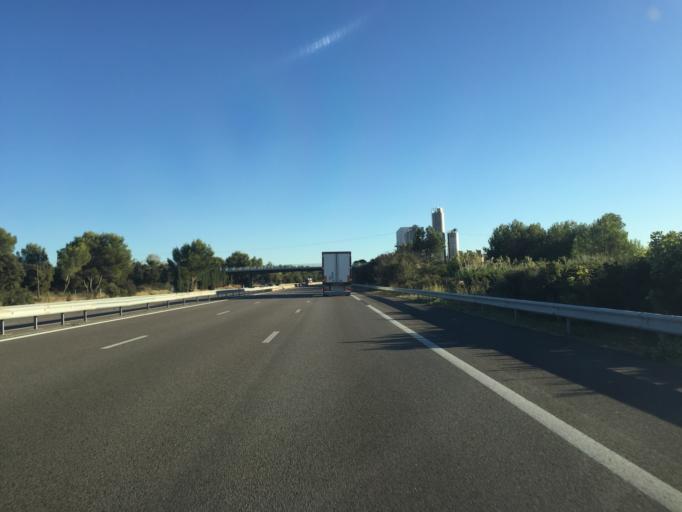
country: FR
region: Provence-Alpes-Cote d'Azur
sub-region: Departement du Vaucluse
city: Sorgues
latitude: 44.0164
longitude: 4.8898
